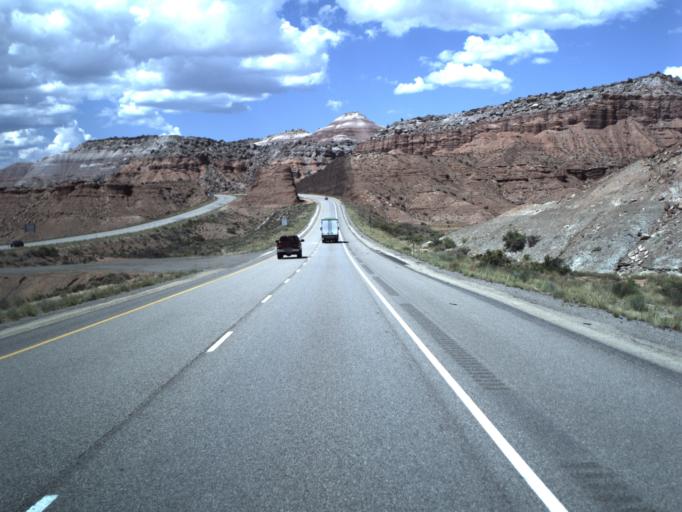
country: US
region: Utah
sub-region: Emery County
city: Ferron
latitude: 38.8315
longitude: -111.1246
